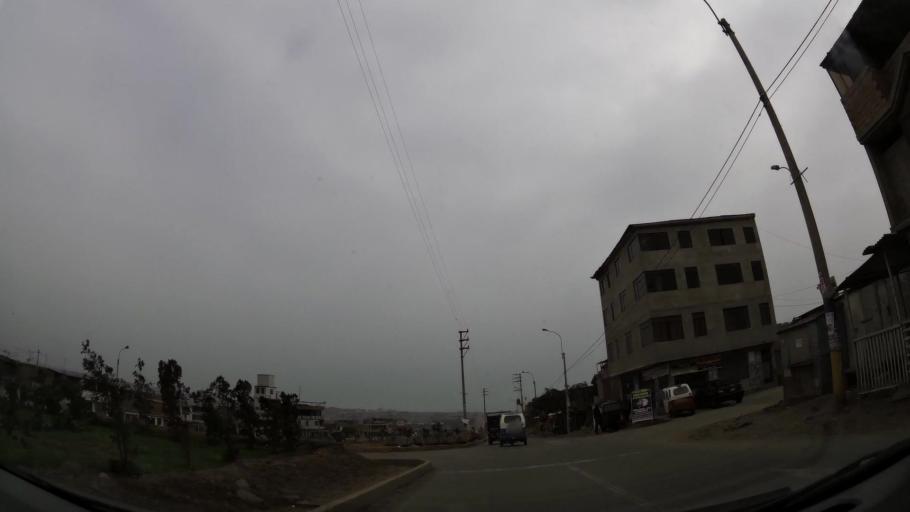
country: PE
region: Lima
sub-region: Lima
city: Surco
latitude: -12.2145
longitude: -76.9511
